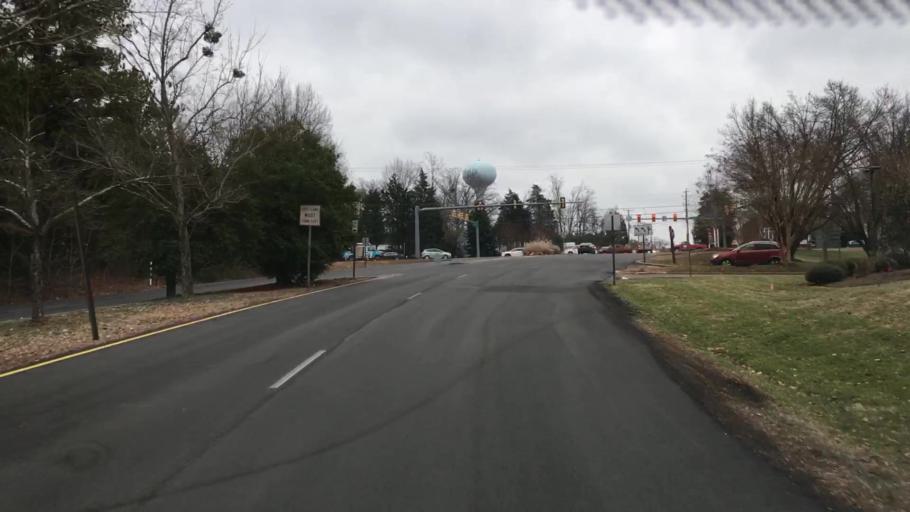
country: US
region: Virginia
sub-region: Chesterfield County
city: Bon Air
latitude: 37.5385
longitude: -77.5629
